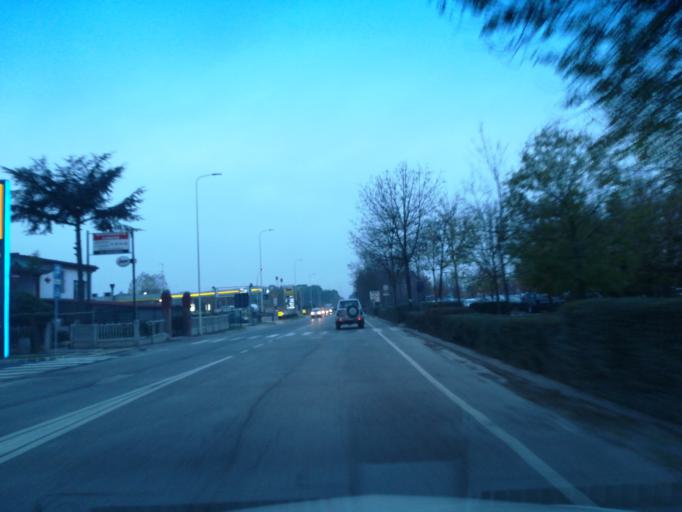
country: IT
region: Emilia-Romagna
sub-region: Provincia di Ravenna
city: Faenza
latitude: 44.2949
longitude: 11.8609
